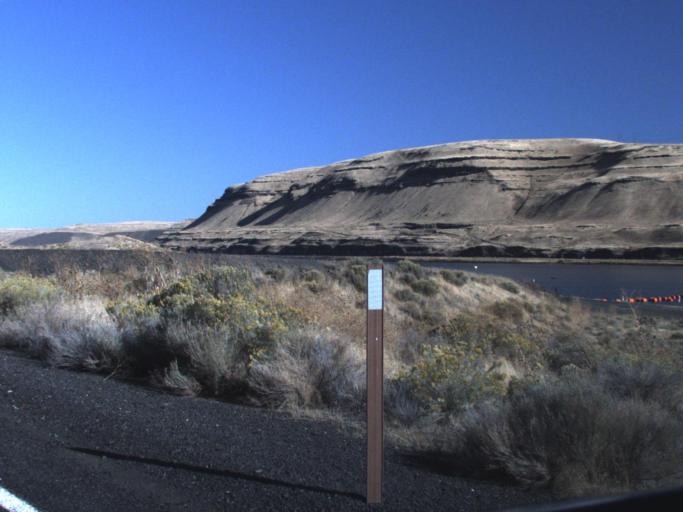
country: US
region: Washington
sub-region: Franklin County
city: Connell
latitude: 46.5668
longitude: -118.5415
